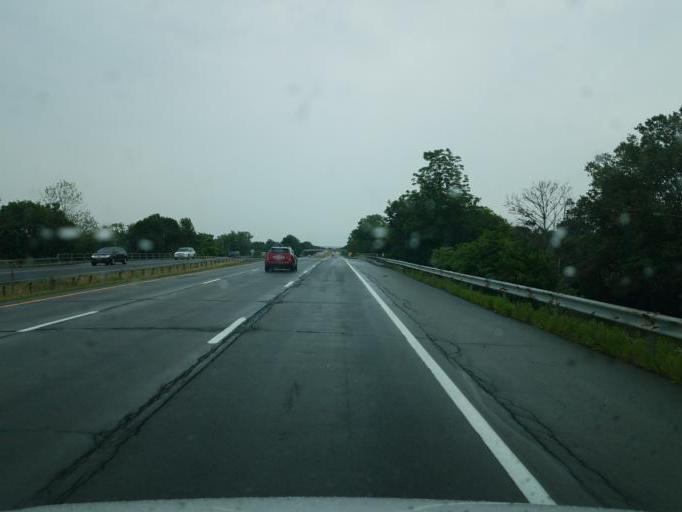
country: US
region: New York
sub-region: Niagara County
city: Niagara Falls
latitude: 43.0796
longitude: -78.9771
